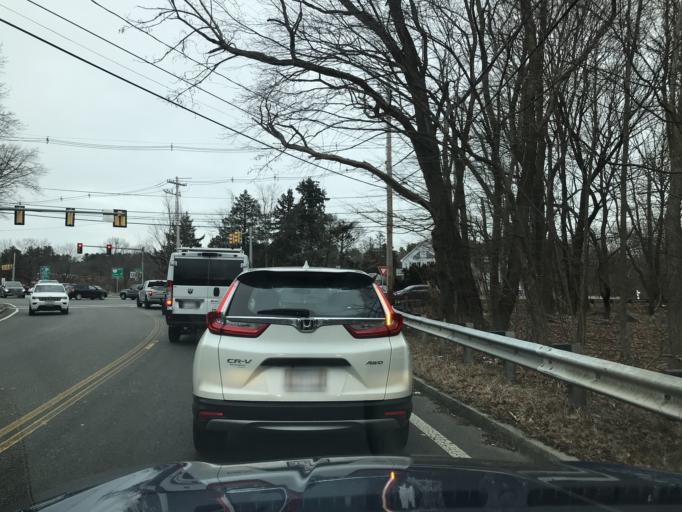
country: US
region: Massachusetts
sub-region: Essex County
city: Lynnfield
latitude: 42.5121
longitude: -71.0280
